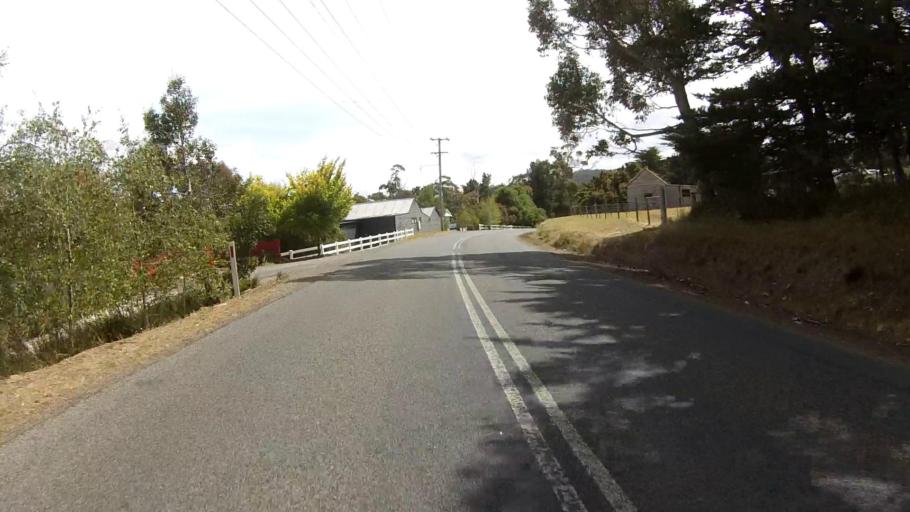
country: AU
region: Tasmania
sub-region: Huon Valley
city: Cygnet
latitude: -43.1955
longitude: 147.1020
